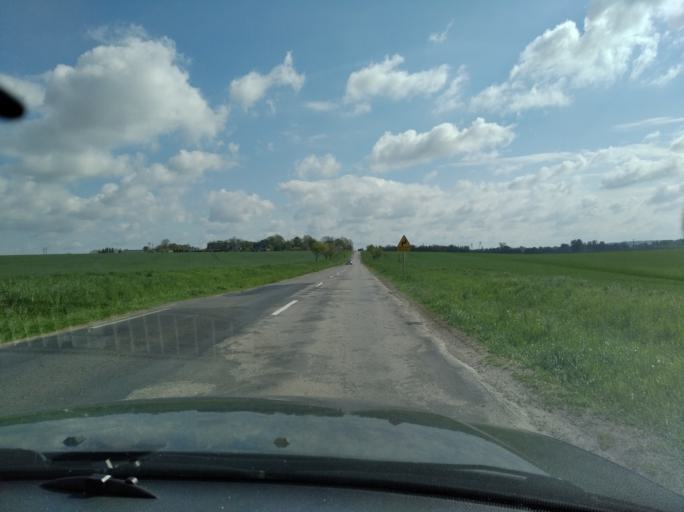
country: PL
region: Subcarpathian Voivodeship
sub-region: Powiat przeworski
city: Kanczuga
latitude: 50.0007
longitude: 22.4309
